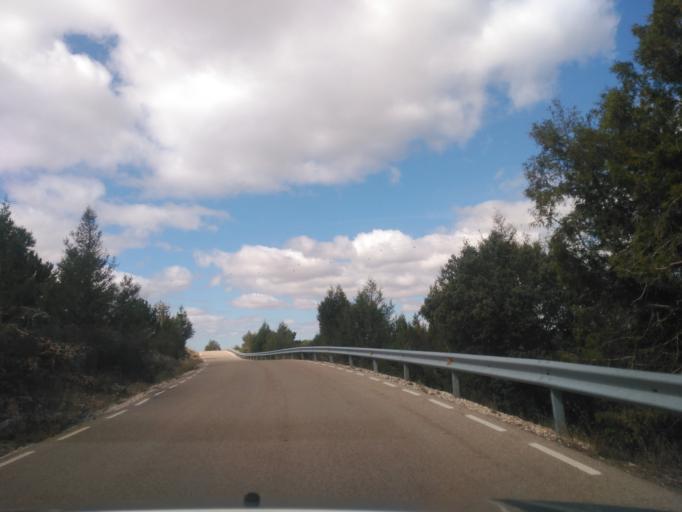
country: ES
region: Castille and Leon
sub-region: Provincia de Soria
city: Espejon
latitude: 41.8393
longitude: -3.2421
